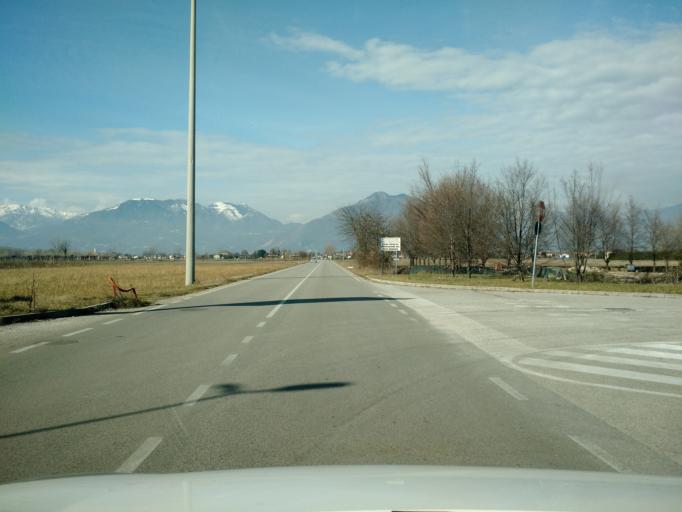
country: IT
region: Veneto
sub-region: Provincia di Vicenza
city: Marano Vicentino
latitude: 45.6803
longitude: 11.4538
